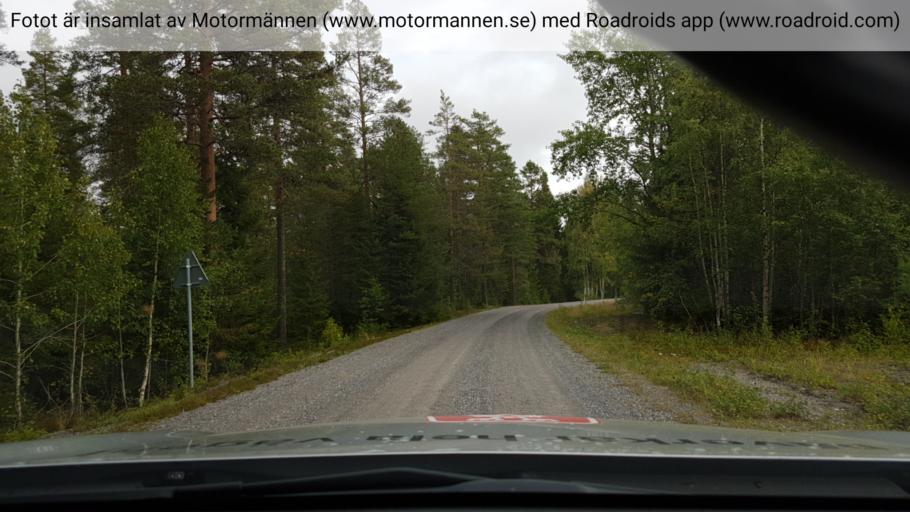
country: SE
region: Vaesterbotten
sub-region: Vannas Kommun
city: Vannasby
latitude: 64.0880
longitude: 20.0486
